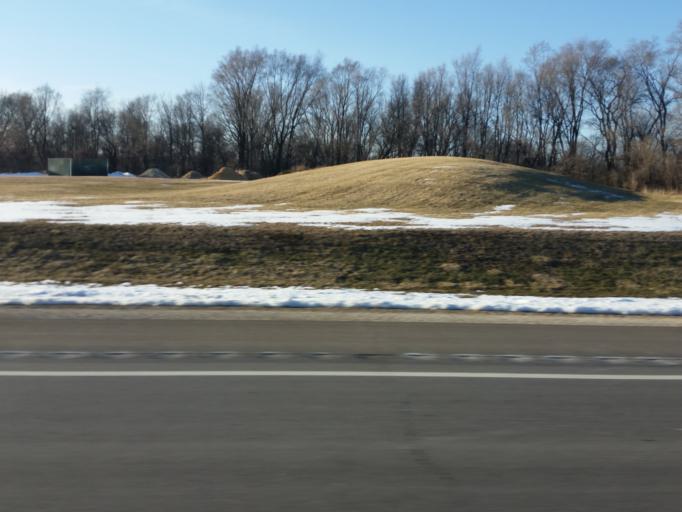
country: US
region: Minnesota
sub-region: Dakota County
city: Farmington
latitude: 44.6564
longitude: -93.1171
